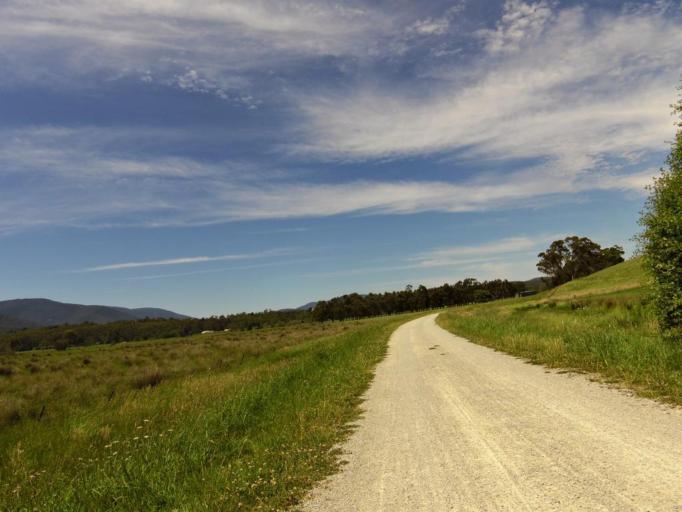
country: AU
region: Victoria
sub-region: Yarra Ranges
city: Woori Yallock
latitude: -37.7651
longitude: 145.5153
